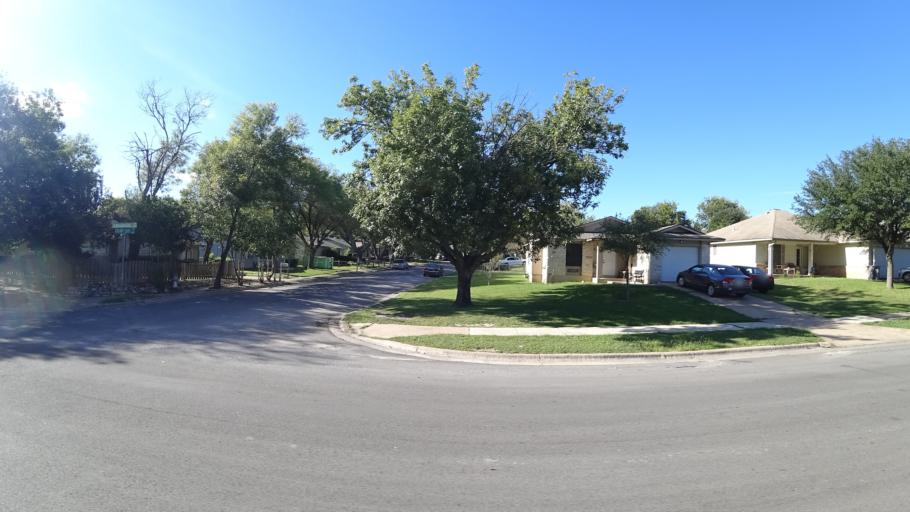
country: US
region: Texas
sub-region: Travis County
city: Hornsby Bend
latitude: 30.3012
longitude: -97.6392
